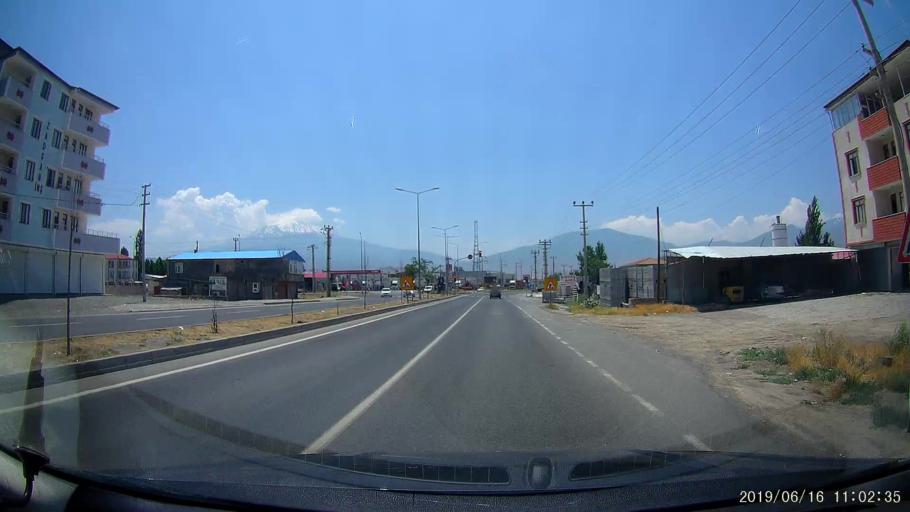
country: TR
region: Igdir
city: Igdir
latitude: 39.9105
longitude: 44.0587
